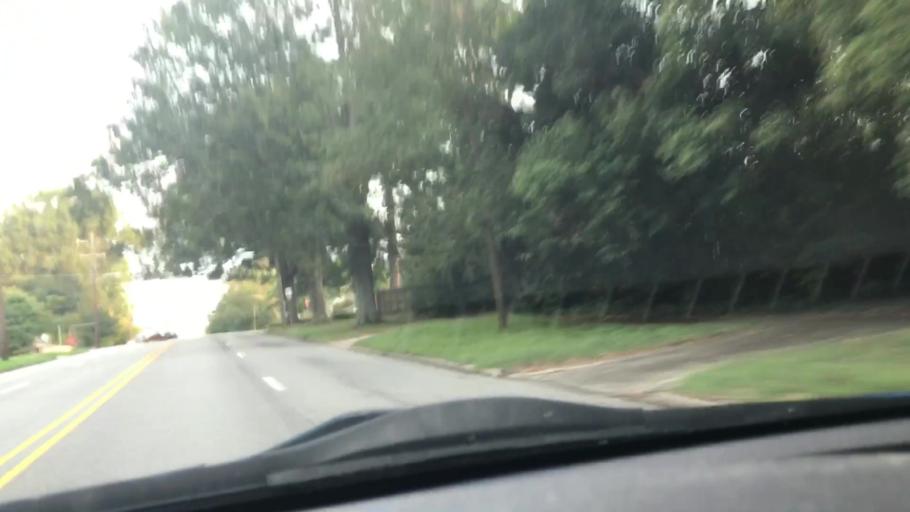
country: US
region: North Carolina
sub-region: Guilford County
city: Greensboro
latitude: 36.0774
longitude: -79.8198
